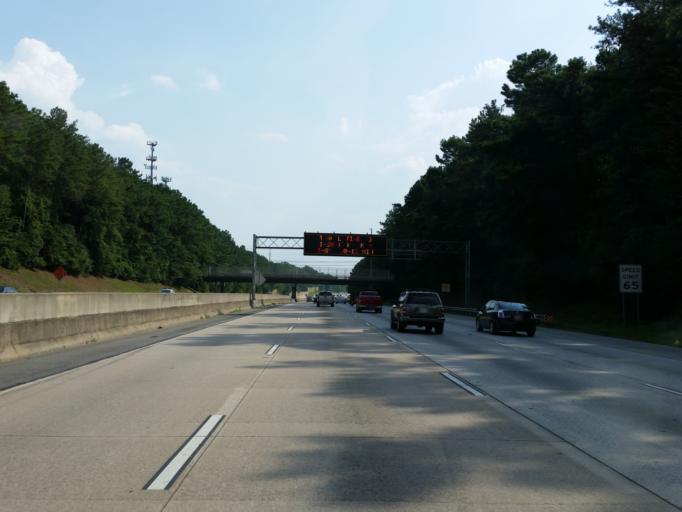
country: US
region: Georgia
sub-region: DeKalb County
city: Dunwoody
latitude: 33.9720
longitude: -84.3470
